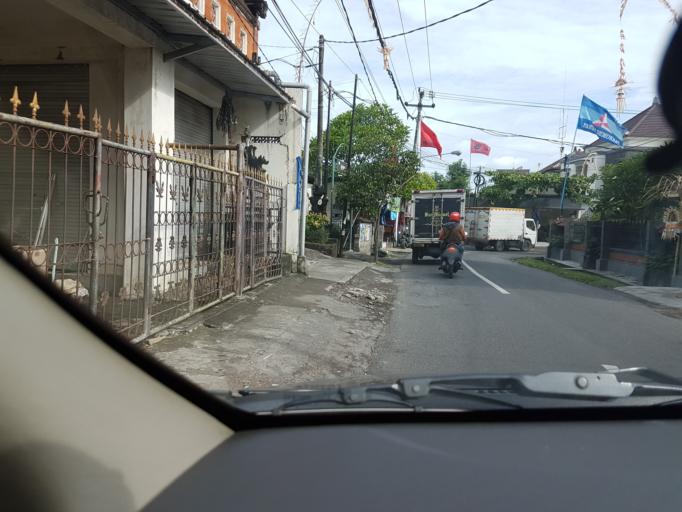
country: ID
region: Bali
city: Denpasar
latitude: -8.6648
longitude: 115.1923
